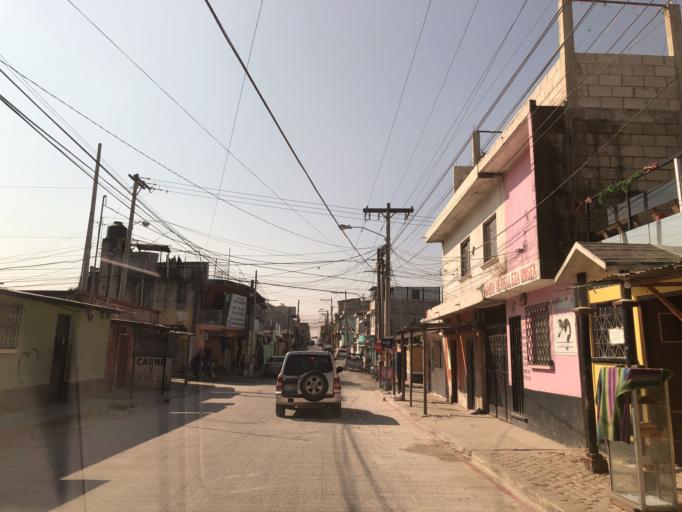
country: GT
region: Guatemala
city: Santa Catarina Pinula
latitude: 14.5441
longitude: -90.5243
